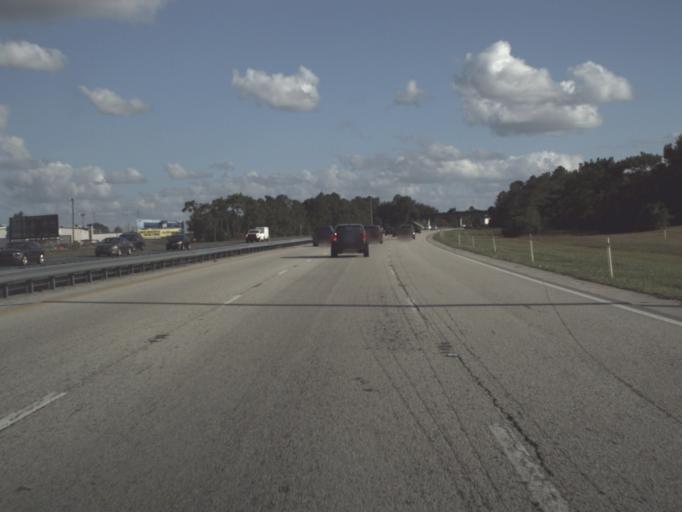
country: US
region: Florida
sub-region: Orange County
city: Taft
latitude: 28.4247
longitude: -81.3969
